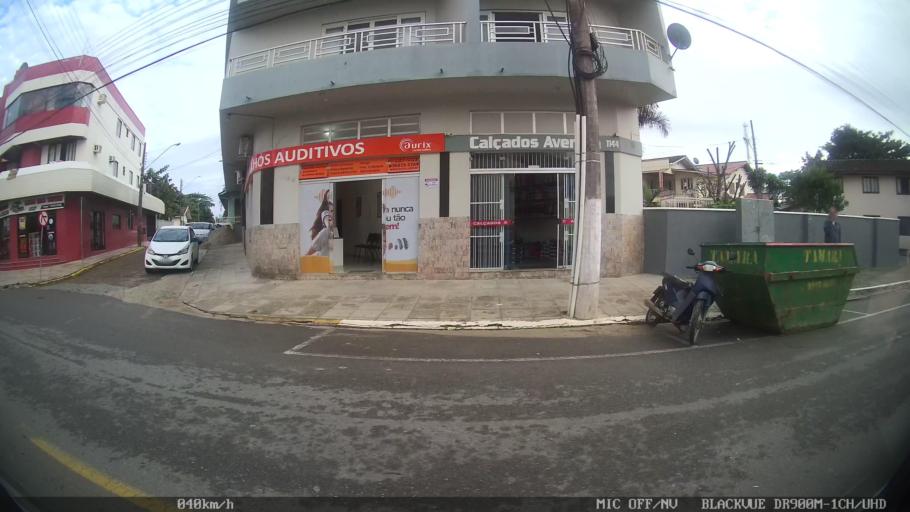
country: BR
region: Santa Catarina
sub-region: Barra Velha
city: Barra Velha
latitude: -26.6420
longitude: -48.6837
